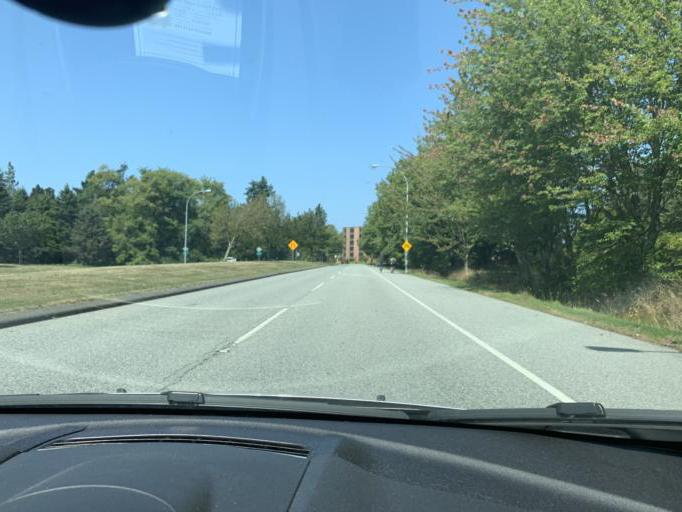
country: CA
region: British Columbia
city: West End
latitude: 49.2550
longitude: -123.2503
